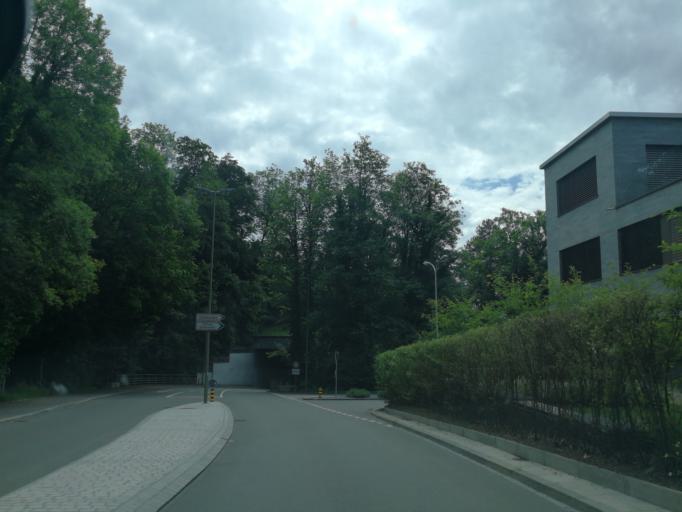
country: CH
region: Zurich
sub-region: Bezirk Meilen
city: Herrliberg
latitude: 47.2842
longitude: 8.6110
